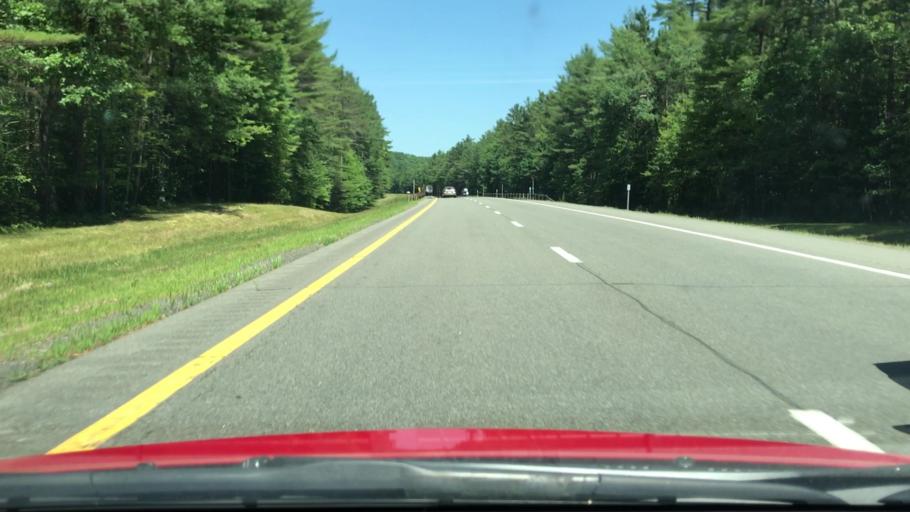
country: US
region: New York
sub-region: Essex County
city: Elizabethtown
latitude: 44.3149
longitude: -73.5282
